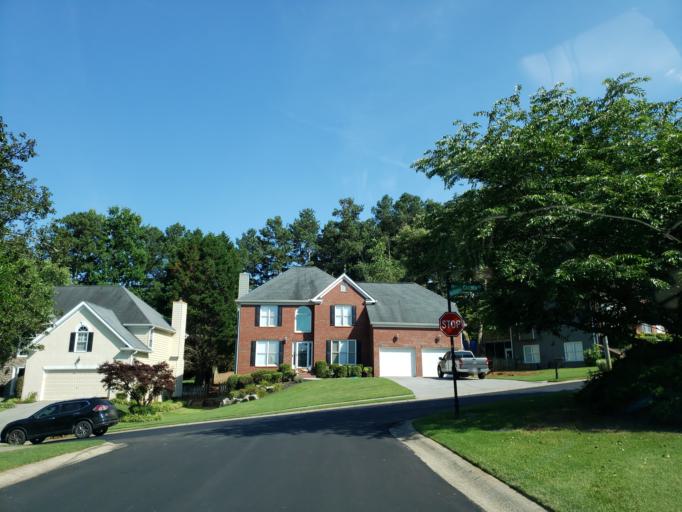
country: US
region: Georgia
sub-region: Cherokee County
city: Woodstock
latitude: 34.1198
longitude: -84.5369
